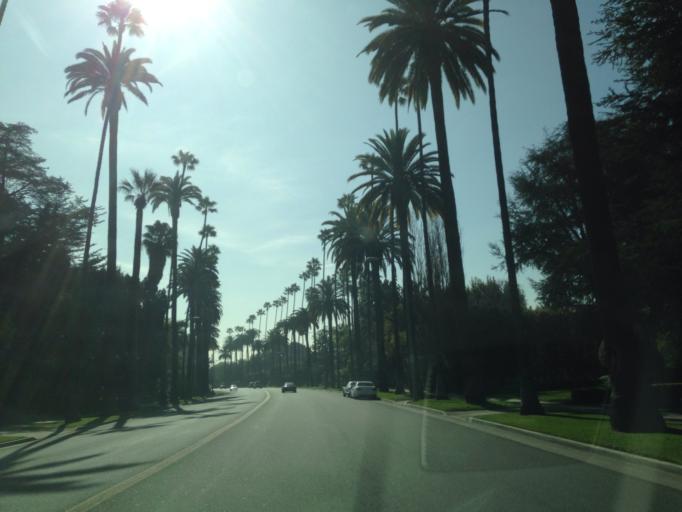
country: US
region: California
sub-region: Los Angeles County
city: Beverly Hills
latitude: 34.0795
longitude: -118.4116
